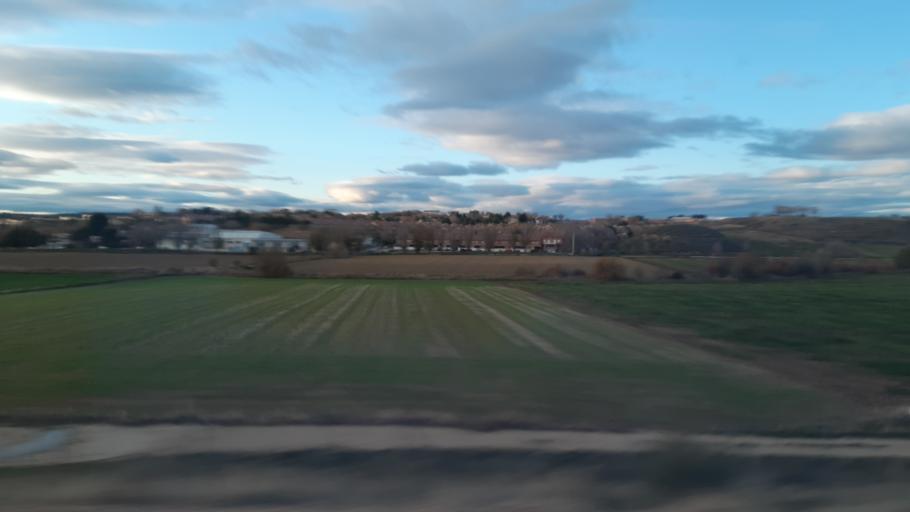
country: ES
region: Madrid
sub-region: Provincia de Madrid
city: Torres de la Alameda
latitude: 40.4401
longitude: -3.3451
